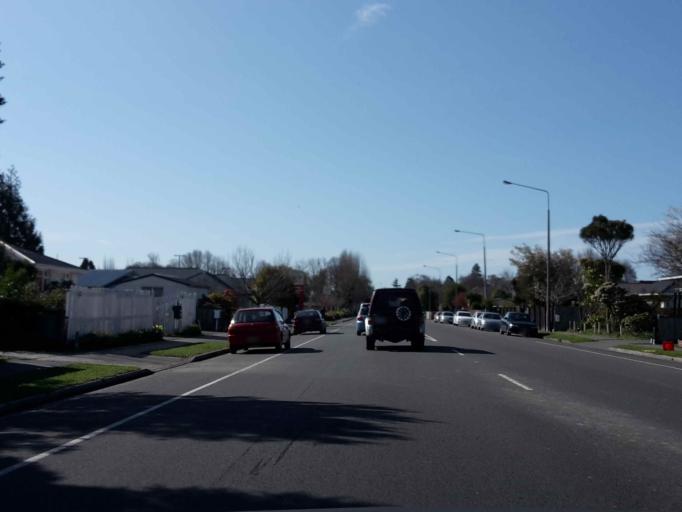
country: NZ
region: Canterbury
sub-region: Christchurch City
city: Christchurch
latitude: -43.5273
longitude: 172.5703
